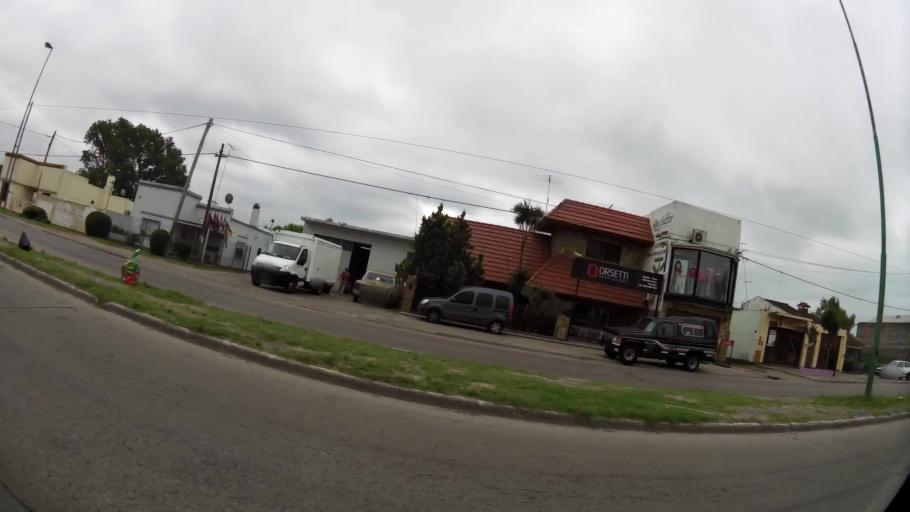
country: AR
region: Buenos Aires
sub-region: Partido de La Plata
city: La Plata
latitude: -34.9857
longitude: -58.0375
